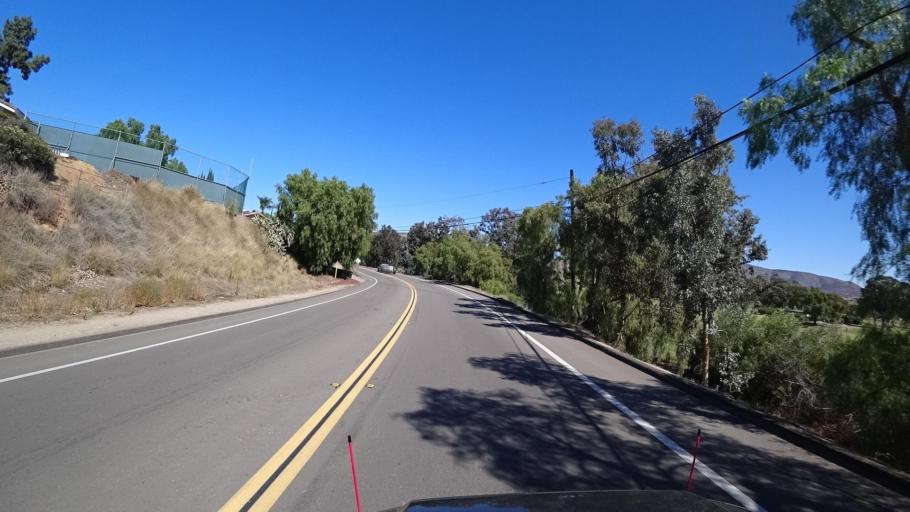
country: US
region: California
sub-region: San Diego County
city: Bonita
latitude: 32.6809
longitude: -117.0147
